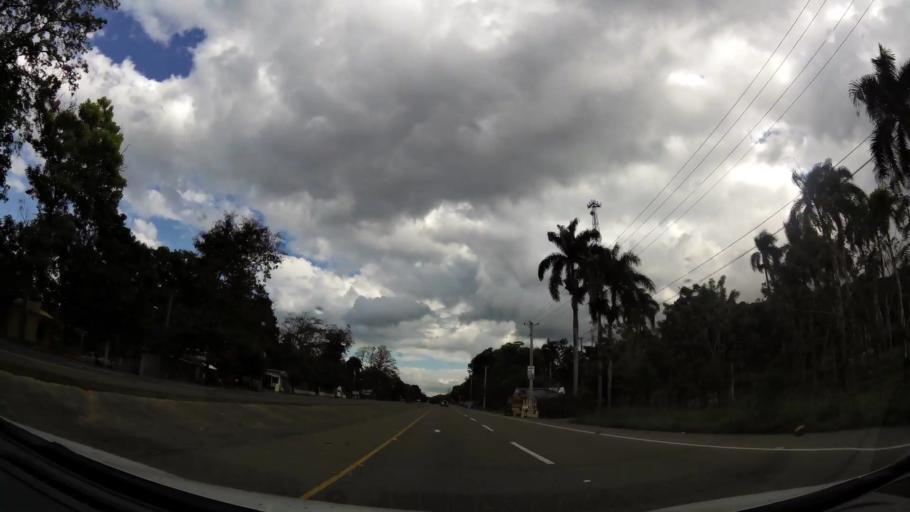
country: DO
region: La Vega
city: Rincon
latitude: 19.1450
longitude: -70.4722
